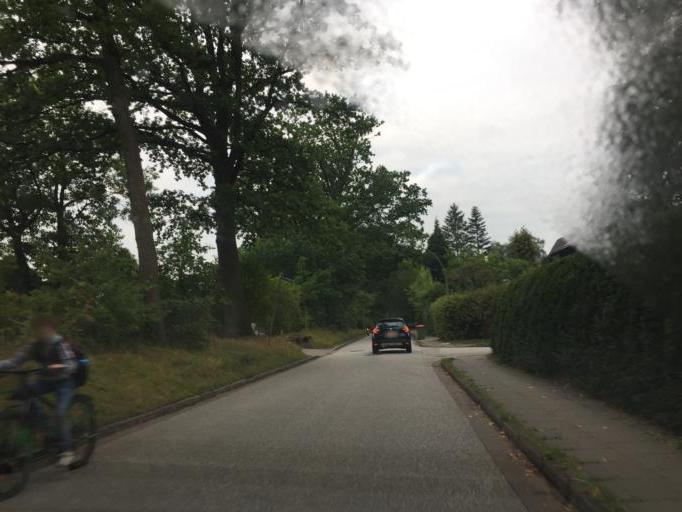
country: DE
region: Hamburg
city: Wellingsbuettel
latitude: 53.6347
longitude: 10.0749
